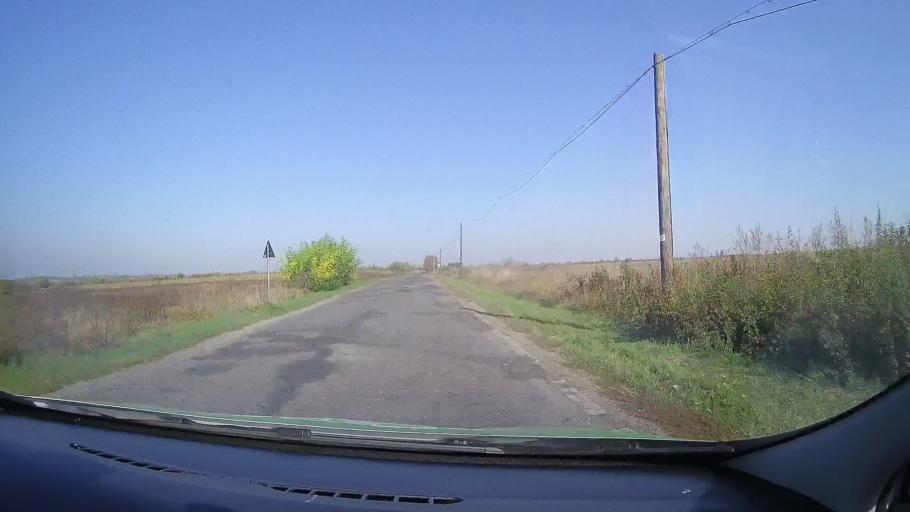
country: RO
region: Satu Mare
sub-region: Comuna Sanislau
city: Sanislau
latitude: 47.6459
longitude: 22.3371
